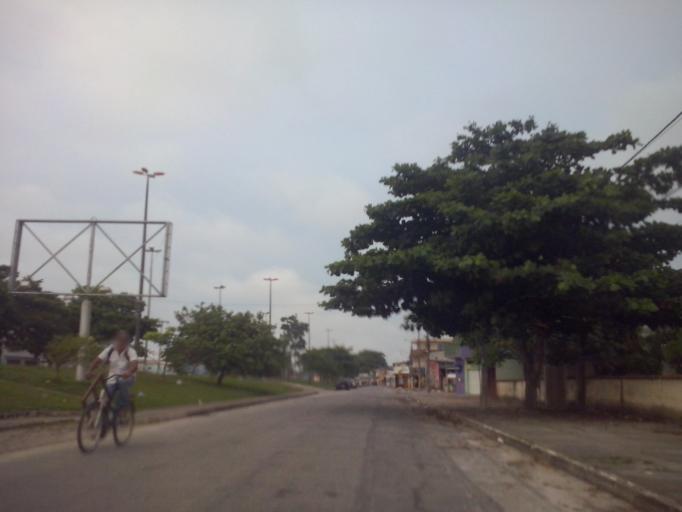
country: BR
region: Rio de Janeiro
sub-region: Rio Das Ostras
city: Rio das Ostras
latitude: -22.5589
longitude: -41.9805
